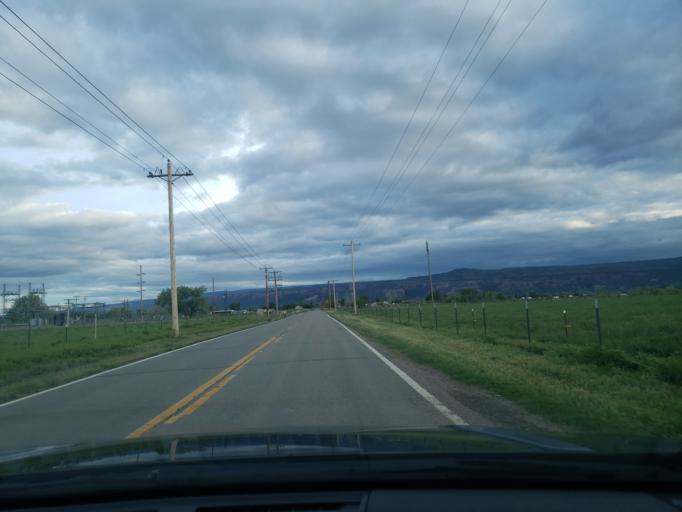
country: US
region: Colorado
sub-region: Mesa County
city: Fruita
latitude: 39.1875
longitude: -108.7013
